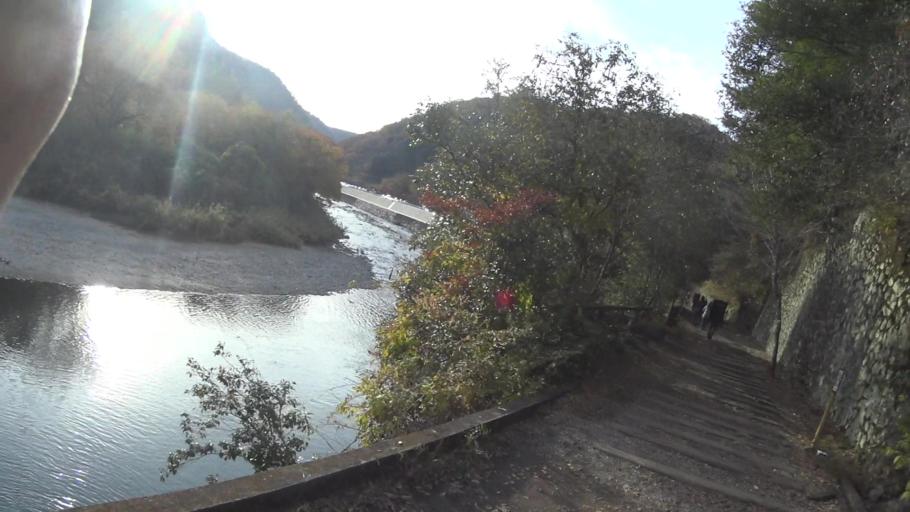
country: JP
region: Hyogo
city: Takarazuka
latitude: 34.8587
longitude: 135.3131
